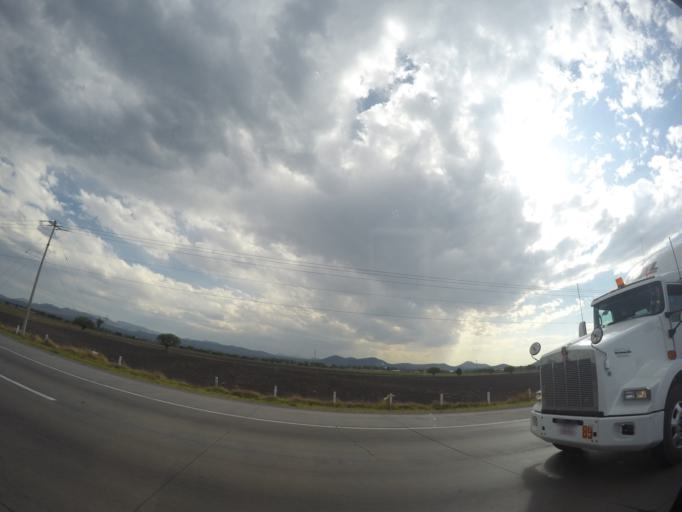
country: MX
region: Queretaro
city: La Estancia
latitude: 20.4468
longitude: -100.0785
